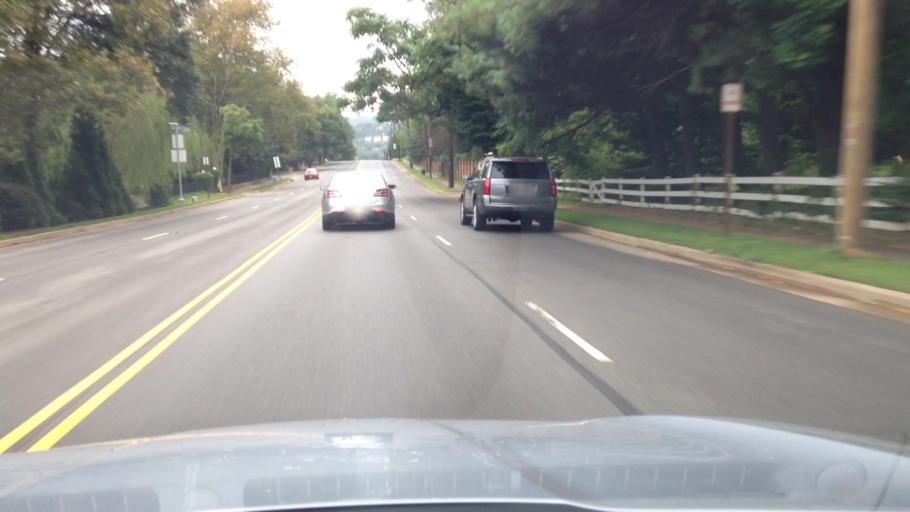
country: US
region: Virginia
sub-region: Fairfax County
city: Huntington
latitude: 38.8133
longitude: -77.0892
